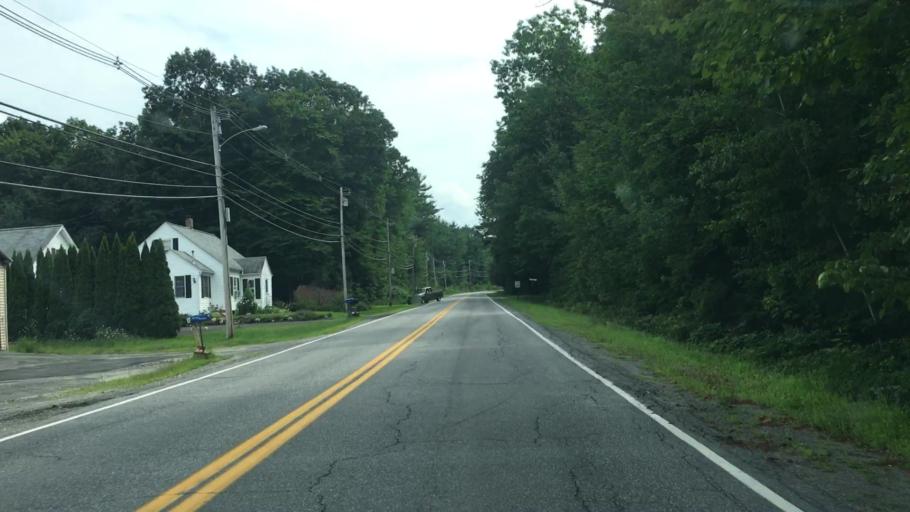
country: US
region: Maine
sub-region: Kennebec County
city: Winslow
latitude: 44.5225
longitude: -69.6310
